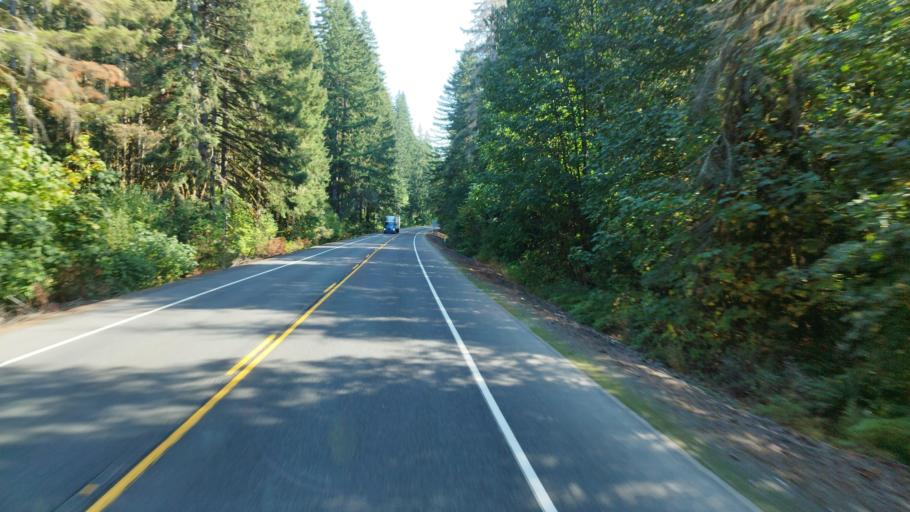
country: US
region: Oregon
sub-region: Columbia County
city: Vernonia
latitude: 45.7755
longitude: -123.3290
